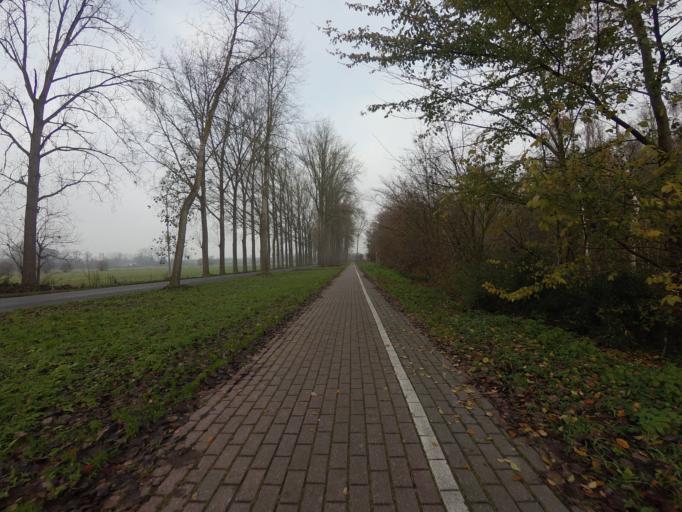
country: BE
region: Flanders
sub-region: Provincie Oost-Vlaanderen
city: Geraardsbergen
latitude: 50.7888
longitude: 3.9060
